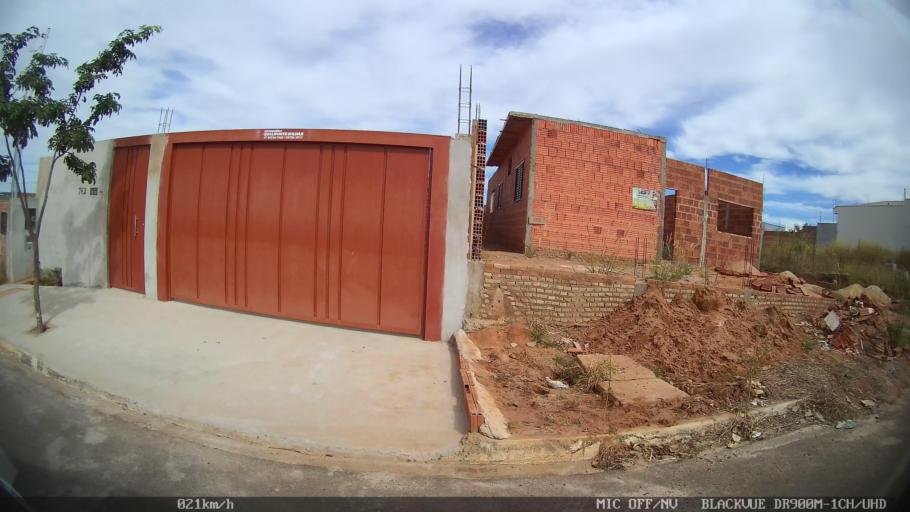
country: BR
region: Sao Paulo
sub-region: Catanduva
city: Catanduva
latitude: -21.1697
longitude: -48.9639
